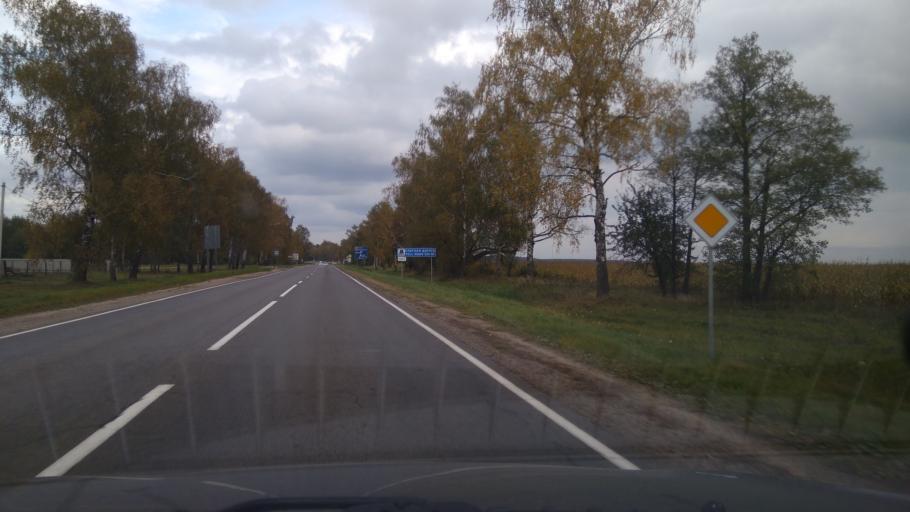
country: BY
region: Minsk
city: Svislach
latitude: 53.6544
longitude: 27.9359
